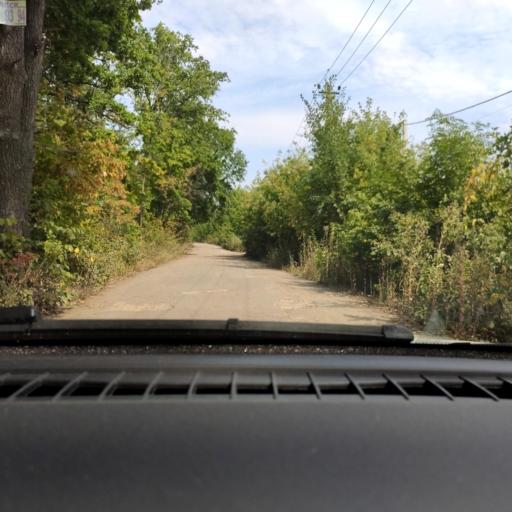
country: RU
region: Voronezj
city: Pridonskoy
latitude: 51.7529
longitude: 39.0784
